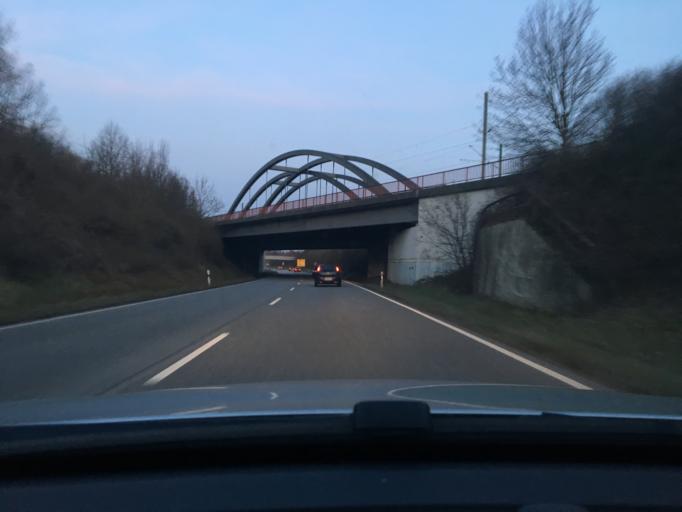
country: DE
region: Rheinland-Pfalz
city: Neustadt
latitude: 49.3595
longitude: 8.1680
